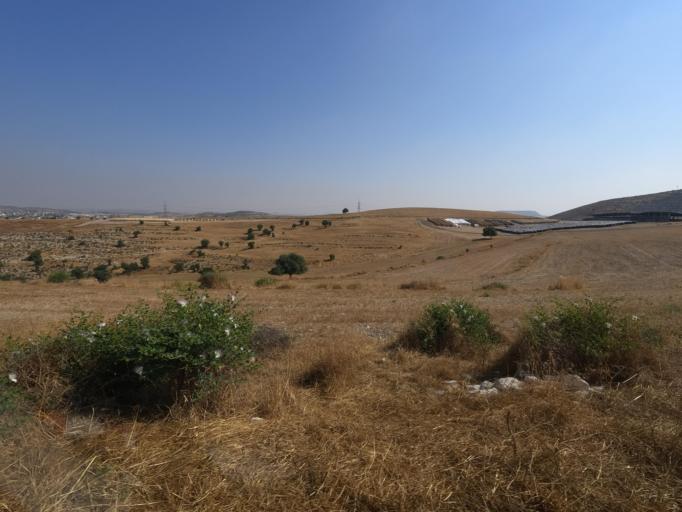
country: CY
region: Lefkosia
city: Lympia
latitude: 34.9811
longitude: 33.4835
